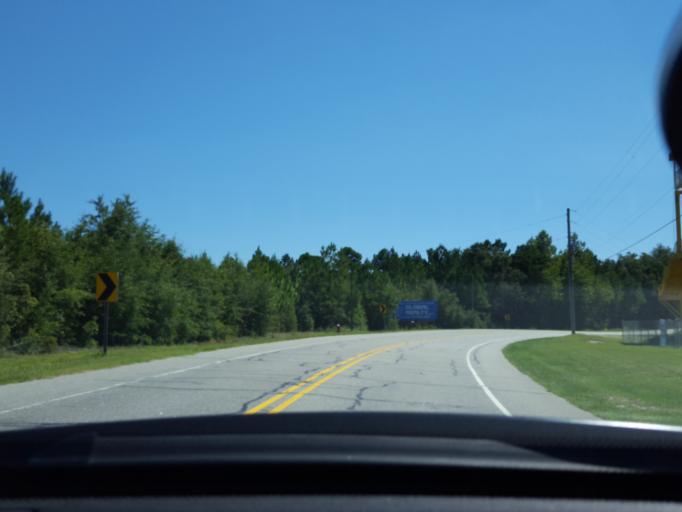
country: US
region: North Carolina
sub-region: Bladen County
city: Elizabethtown
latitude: 34.6483
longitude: -78.5199
